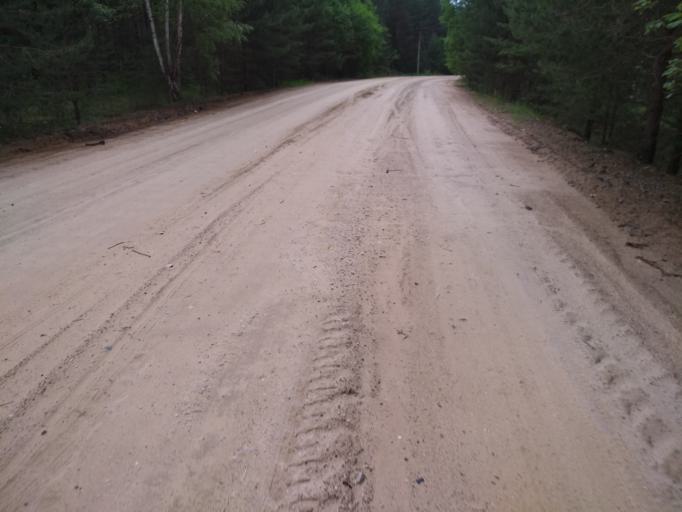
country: RU
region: Tverskaya
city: Vyshniy Volochek
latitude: 57.5080
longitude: 34.4727
